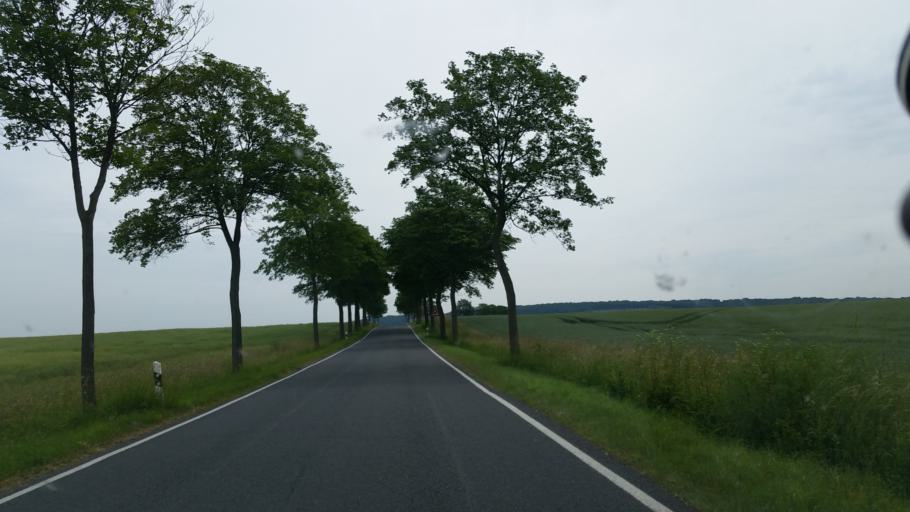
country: DE
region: Lower Saxony
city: Lehre
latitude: 52.2959
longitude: 10.7318
